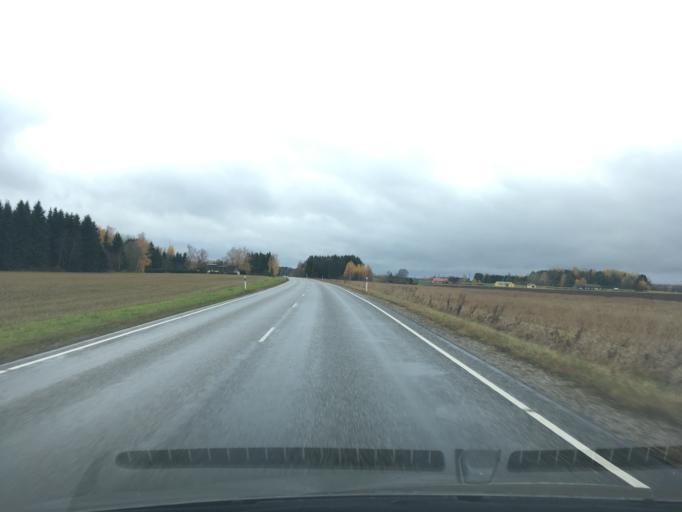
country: EE
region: Jogevamaa
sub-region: Tabivere vald
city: Tabivere
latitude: 58.4705
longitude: 26.5961
